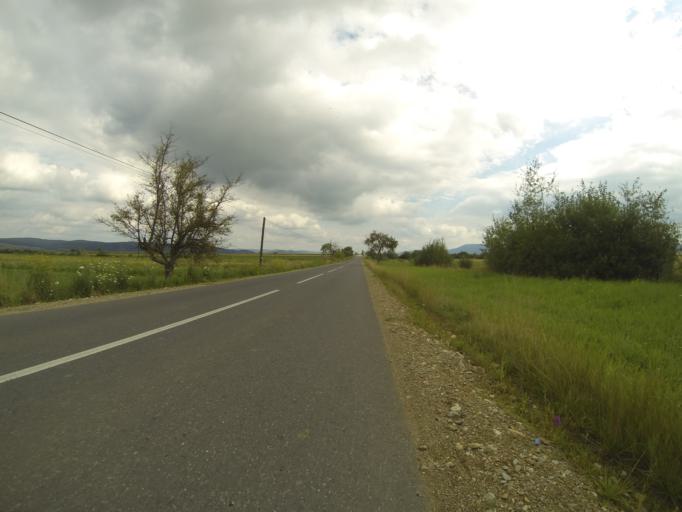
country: RO
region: Brasov
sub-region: Comuna Parau
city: Parau
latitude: 45.8521
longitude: 25.1936
